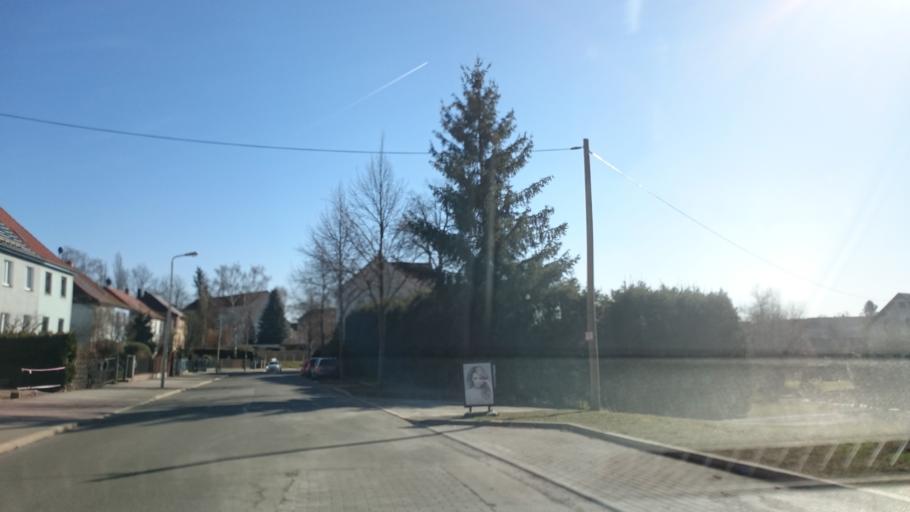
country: DE
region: Saxony
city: Lichtentanne
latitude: 50.7270
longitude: 12.4414
